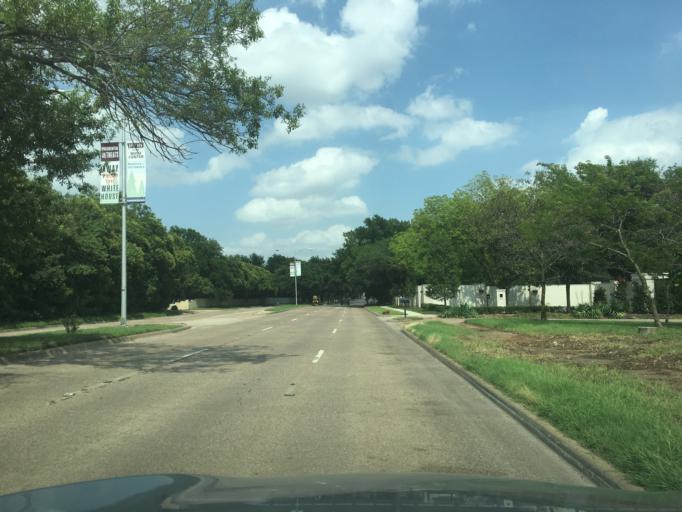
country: US
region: Texas
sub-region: Dallas County
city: University Park
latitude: 32.8944
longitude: -96.8194
